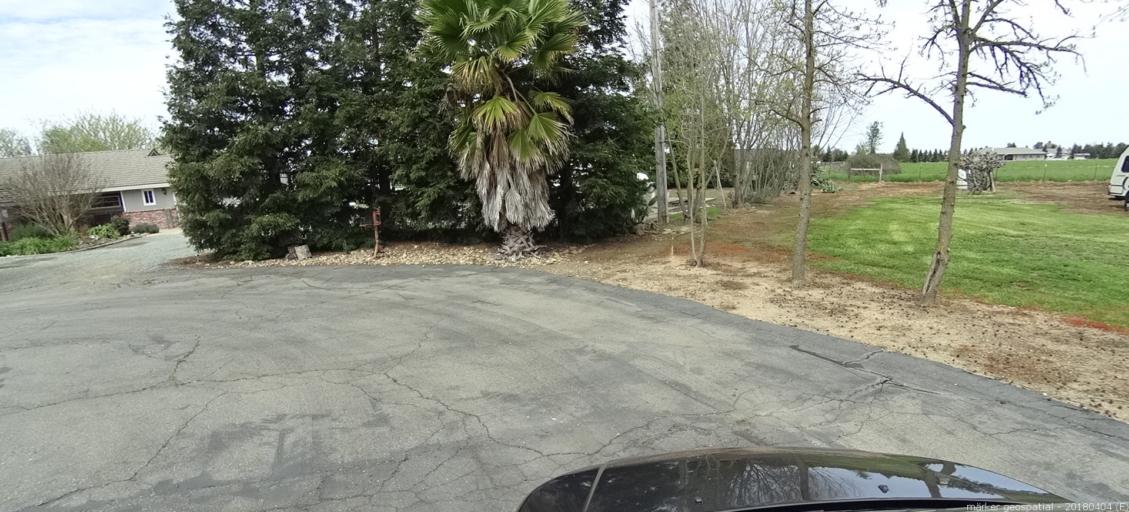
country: US
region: California
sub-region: Sacramento County
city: Herald
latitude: 38.2808
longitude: -121.2311
